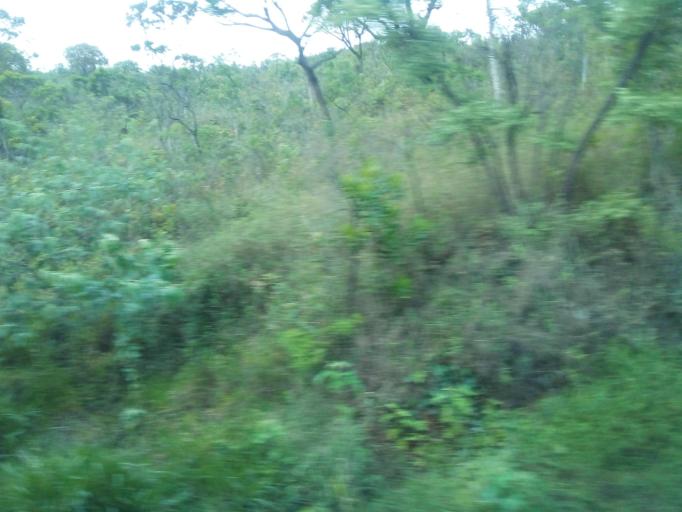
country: BR
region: Minas Gerais
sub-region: Caete
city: Caete
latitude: -19.9085
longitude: -43.7108
